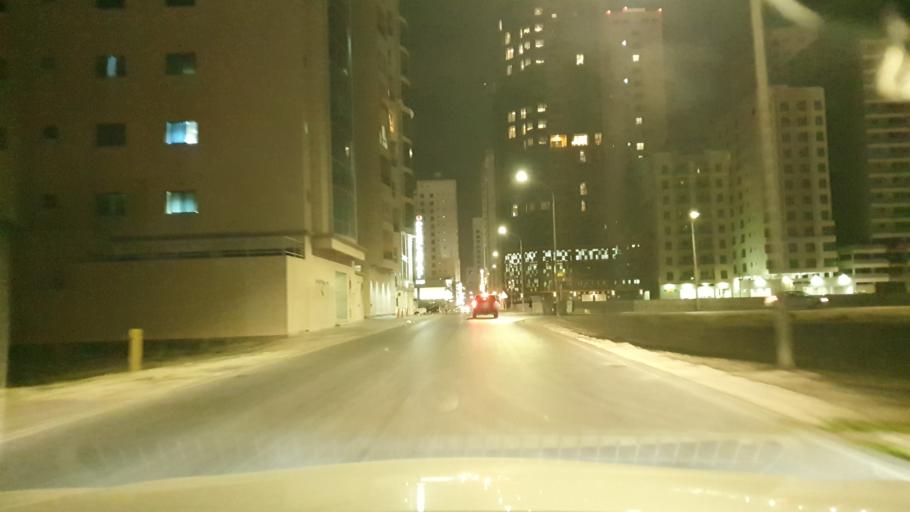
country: BH
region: Manama
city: Manama
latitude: 26.2184
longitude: 50.6018
